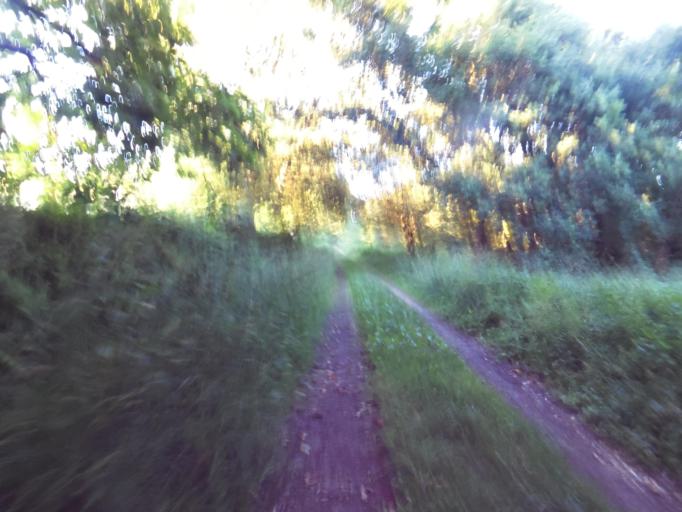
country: FR
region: Brittany
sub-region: Departement du Morbihan
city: Molac
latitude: 47.7175
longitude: -2.4286
